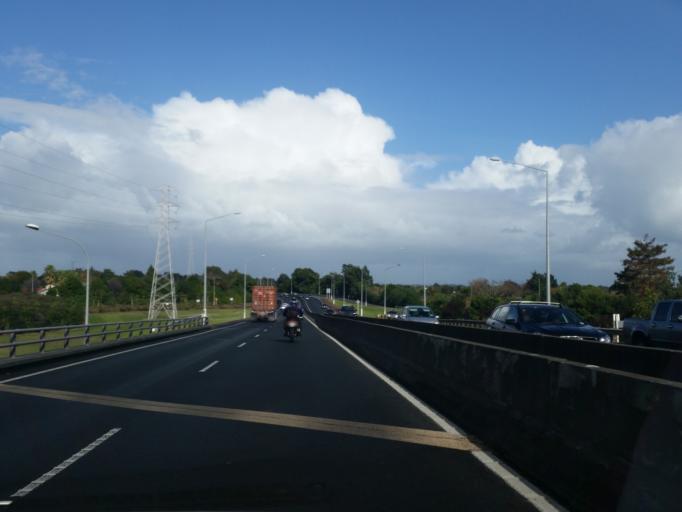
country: NZ
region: Auckland
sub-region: Auckland
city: Takanini
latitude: -37.0362
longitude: 174.9102
